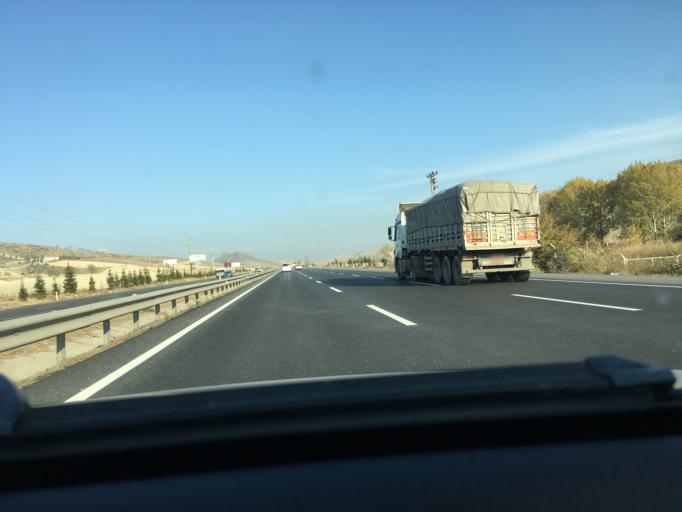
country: TR
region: Ankara
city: Temelli
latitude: 39.7611
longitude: 32.4645
